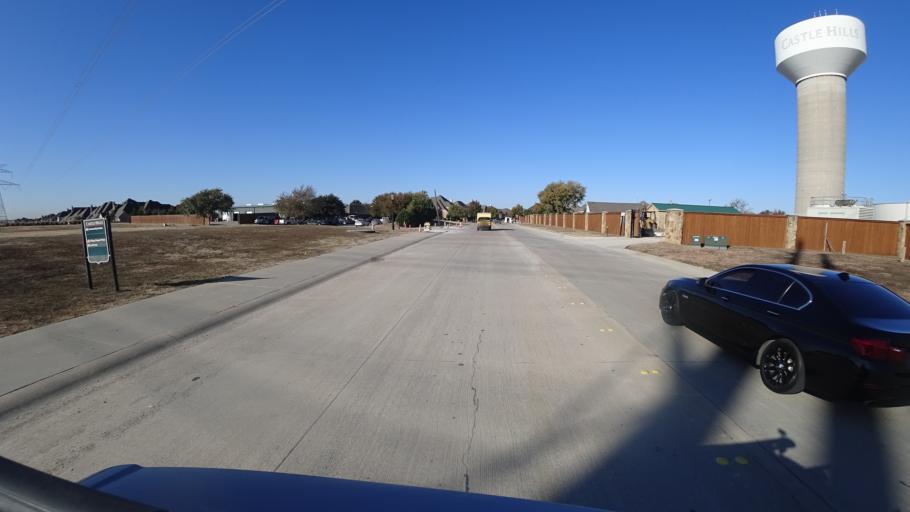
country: US
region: Texas
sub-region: Denton County
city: The Colony
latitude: 33.0427
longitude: -96.9073
